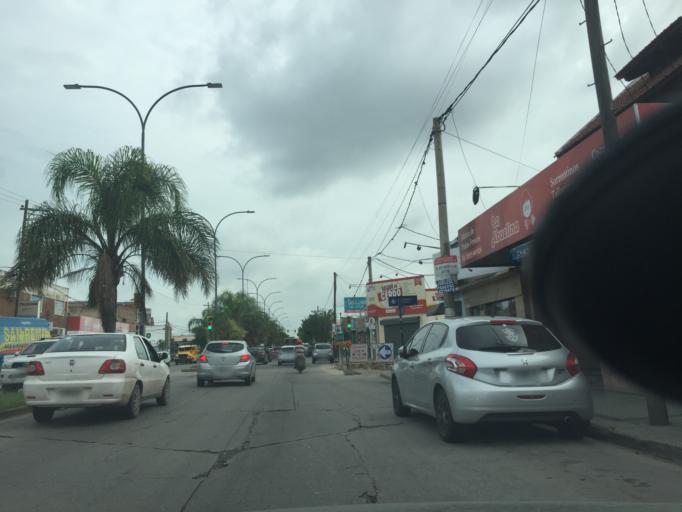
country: AR
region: Cordoba
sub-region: Departamento de Capital
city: Cordoba
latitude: -31.4479
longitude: -64.1992
